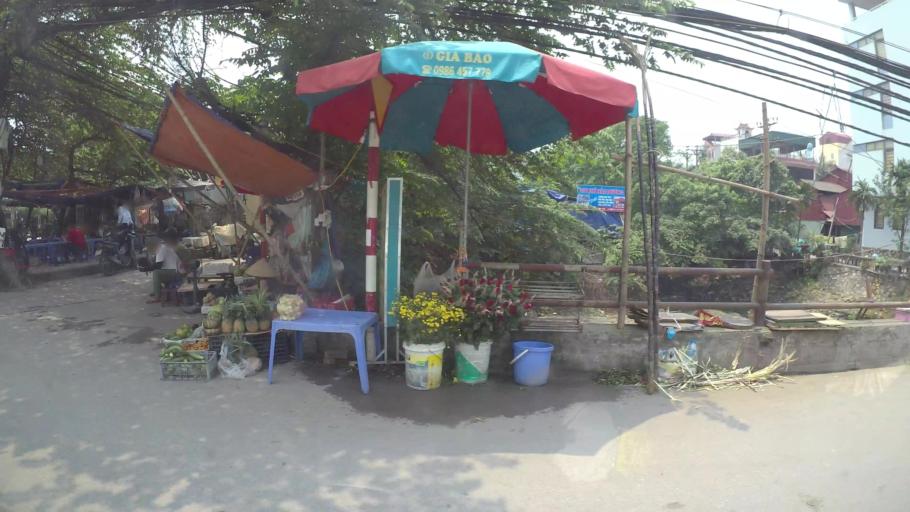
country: VN
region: Ha Noi
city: Ha Dong
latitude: 20.9937
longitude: 105.7773
